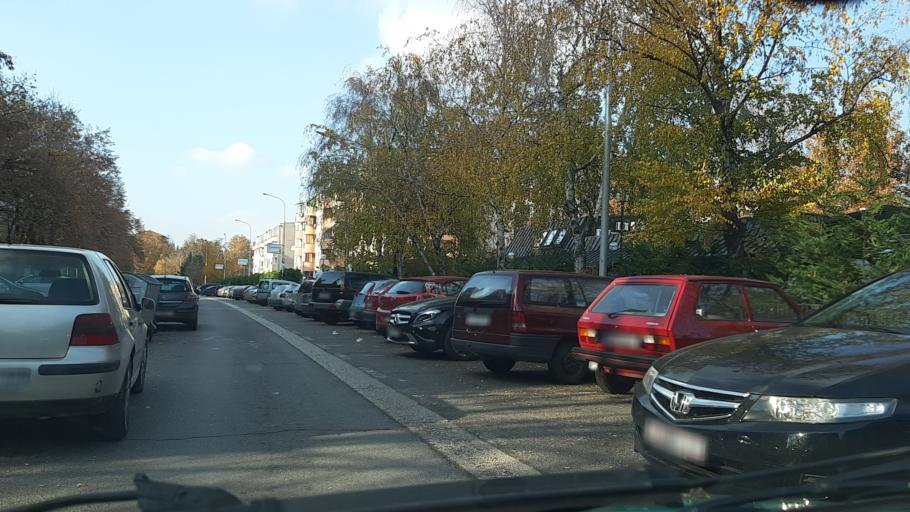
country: MK
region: Kisela Voda
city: Usje
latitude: 41.9858
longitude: 21.4642
